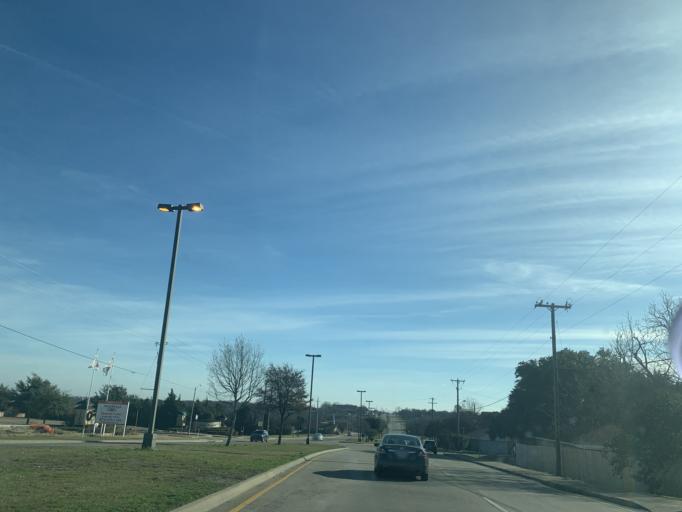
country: US
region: Texas
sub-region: Dallas County
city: DeSoto
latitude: 32.5897
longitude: -96.8670
